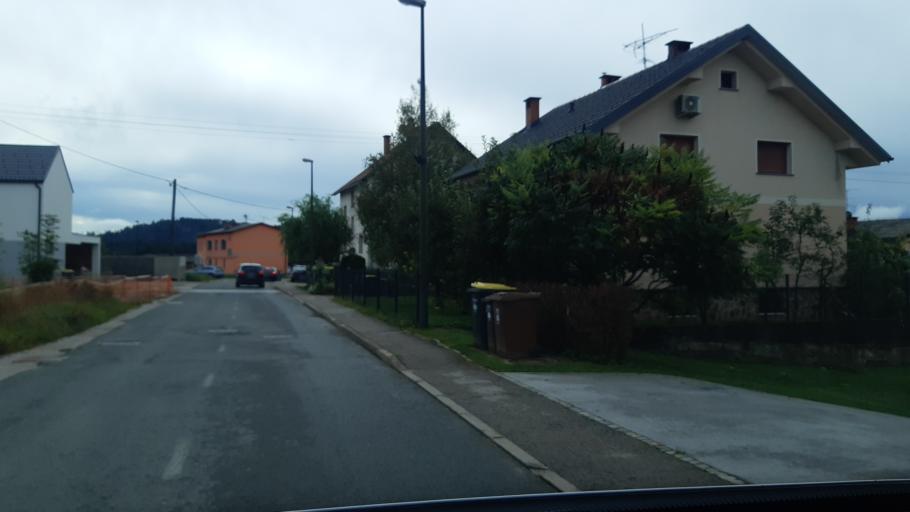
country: SI
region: Vodice
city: Vodice
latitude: 46.1903
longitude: 14.4985
